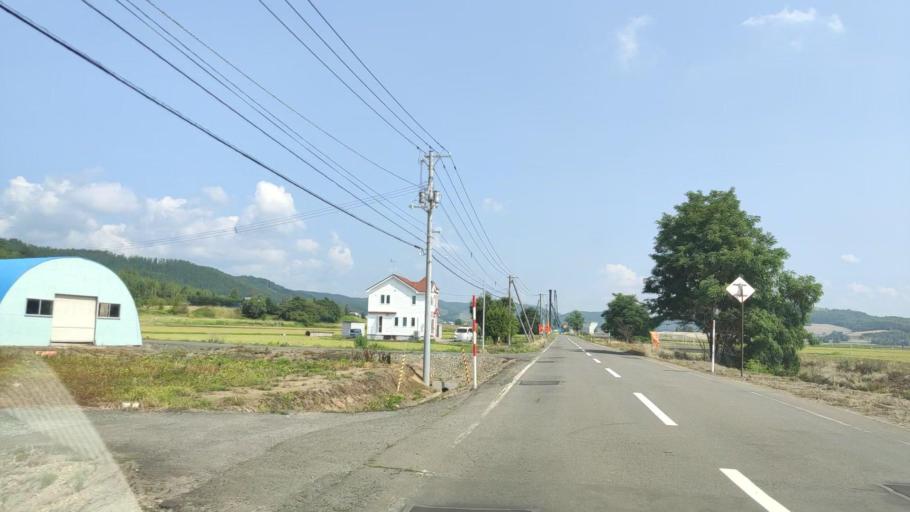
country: JP
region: Hokkaido
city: Shimo-furano
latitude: 43.3838
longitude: 142.3925
